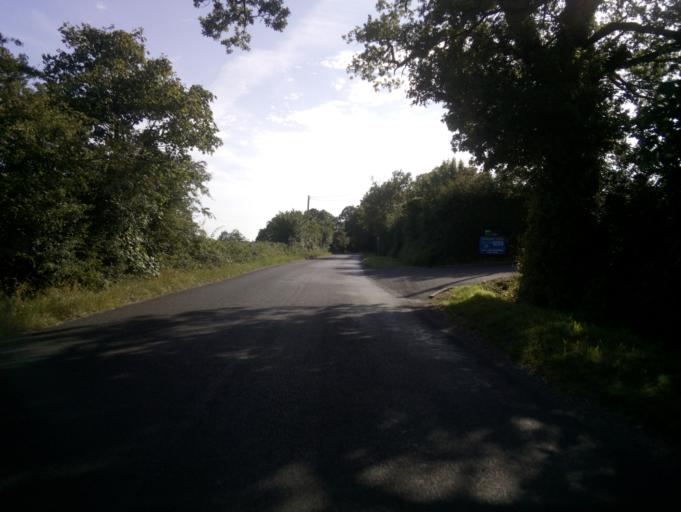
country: GB
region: England
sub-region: Hampshire
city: Chandlers Ford
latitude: 50.9875
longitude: -1.4153
